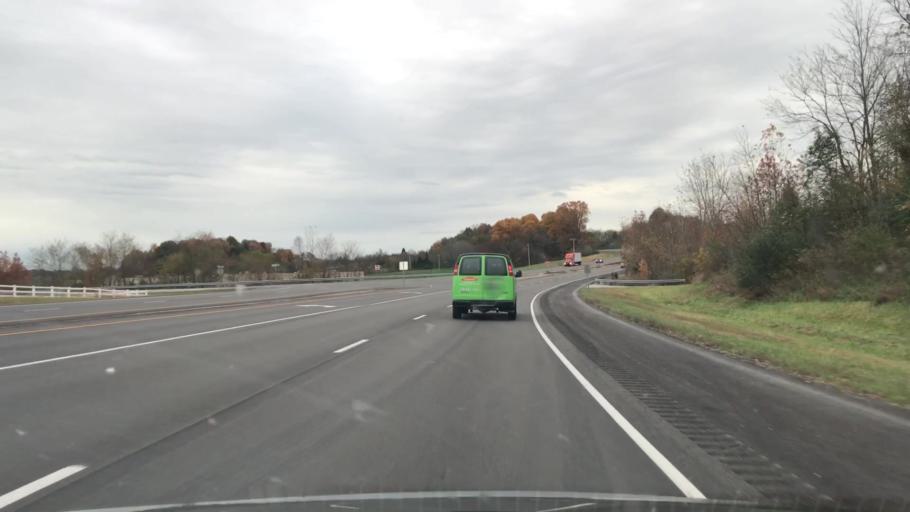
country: US
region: Kentucky
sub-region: Barren County
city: Glasgow
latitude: 37.0270
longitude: -85.9312
